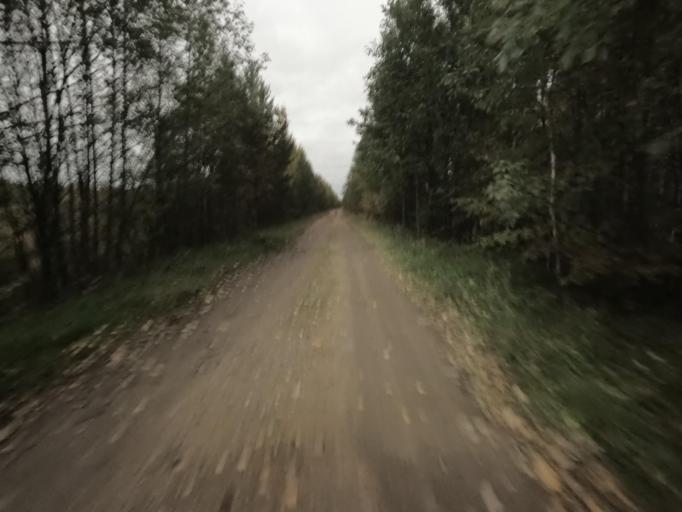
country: RU
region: Leningrad
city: Kirovsk
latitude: 59.8334
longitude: 30.9803
